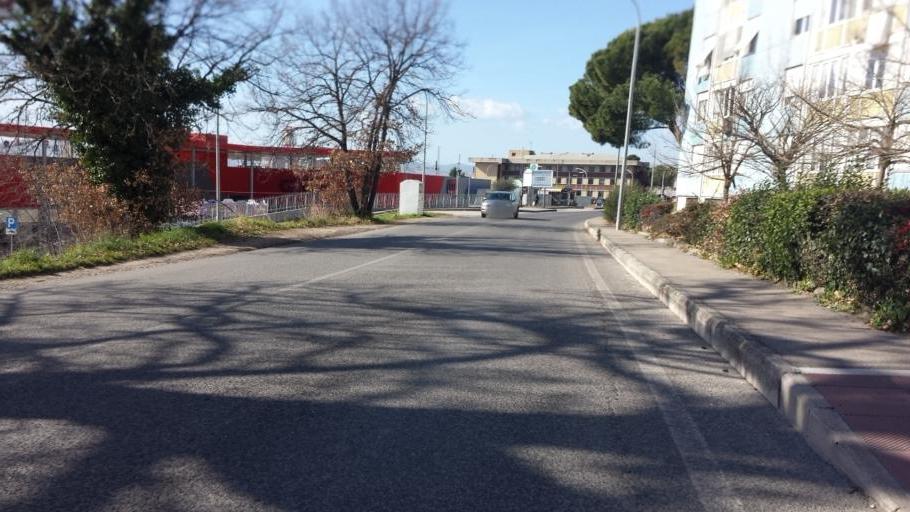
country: IT
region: Umbria
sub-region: Provincia di Terni
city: Terni
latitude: 42.5883
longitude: 12.6044
